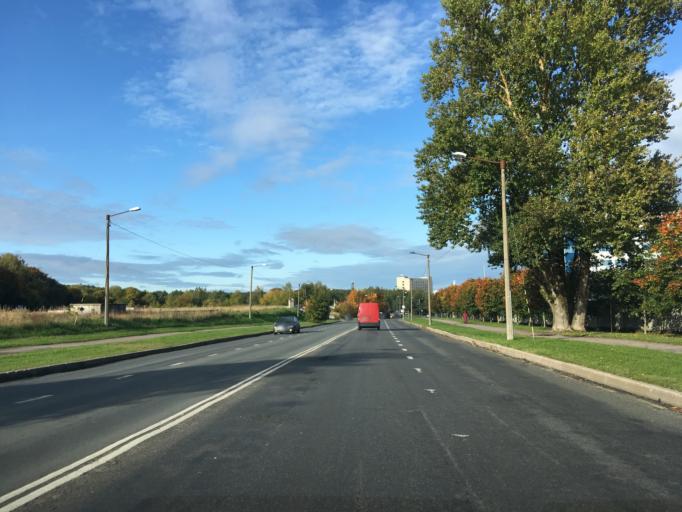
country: EE
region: Harju
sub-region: Tallinna linn
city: Tallinn
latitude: 59.3946
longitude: 24.7075
